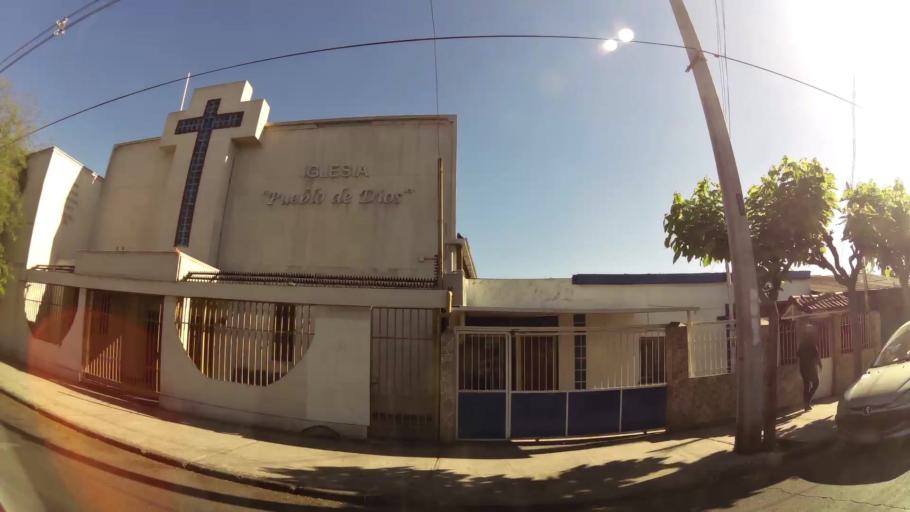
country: CL
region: Santiago Metropolitan
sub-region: Provincia de Maipo
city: San Bernardo
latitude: -33.5501
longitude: -70.6850
